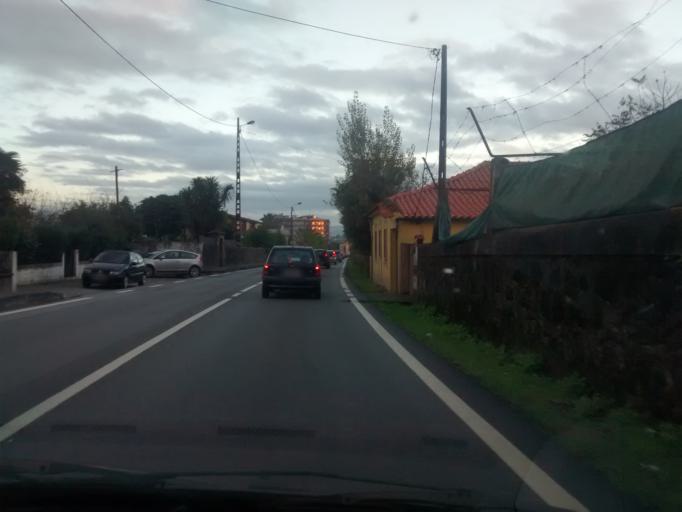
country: PT
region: Braga
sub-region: Vila Verde
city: Prado
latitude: 41.6030
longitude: -8.4673
